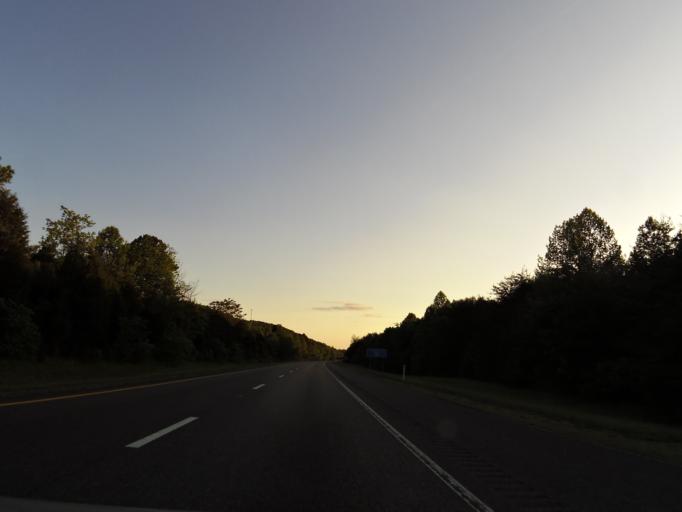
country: US
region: Tennessee
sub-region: Washington County
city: Fall Branch
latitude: 36.3703
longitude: -82.6779
